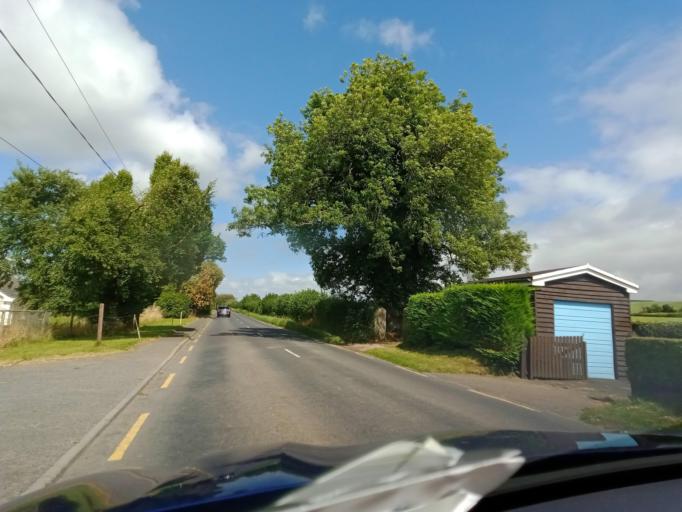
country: IE
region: Leinster
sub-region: Laois
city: Abbeyleix
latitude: 52.9530
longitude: -7.3026
